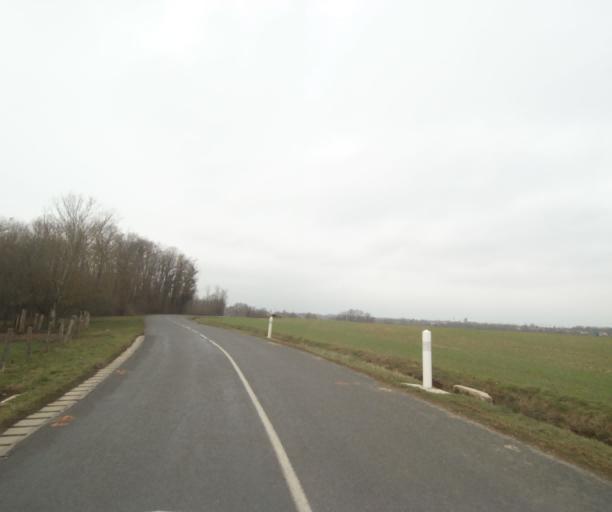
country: FR
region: Champagne-Ardenne
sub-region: Departement de la Marne
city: Pargny-sur-Saulx
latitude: 48.7378
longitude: 4.8584
